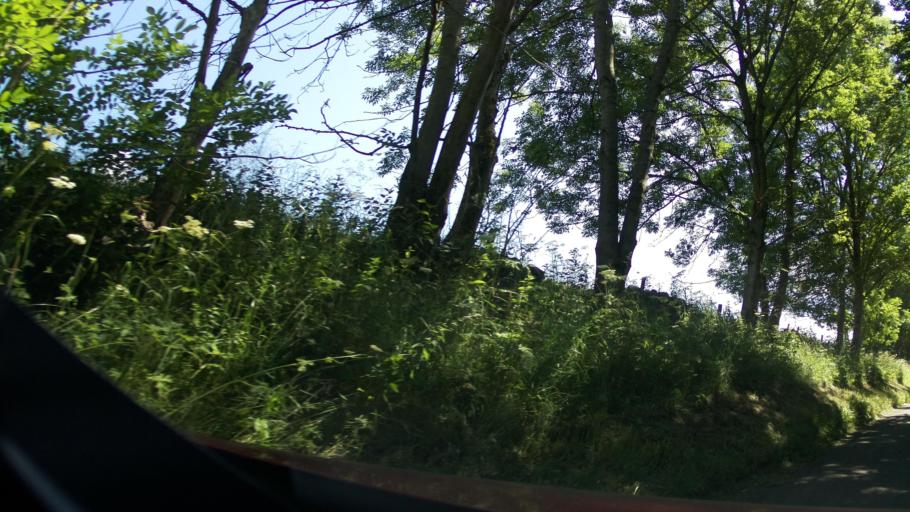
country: GB
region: England
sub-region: Derbyshire
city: Buxton
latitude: 53.2864
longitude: -1.8601
